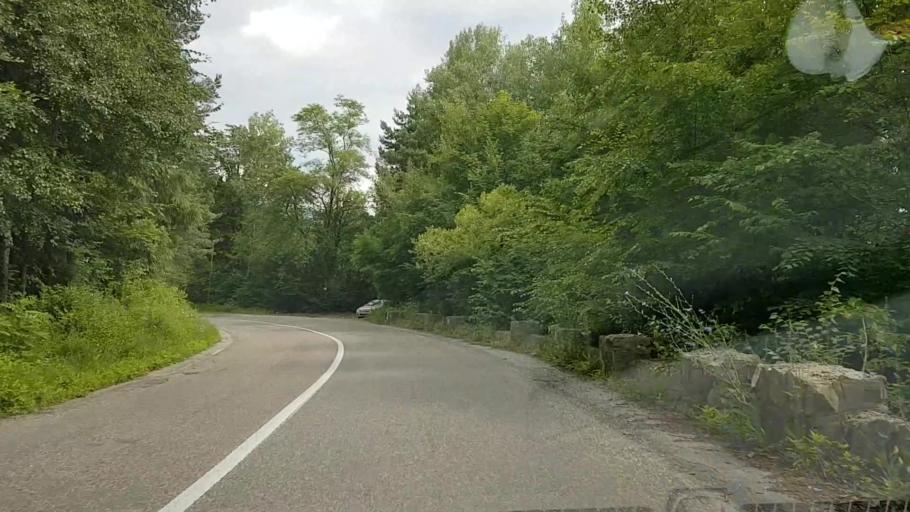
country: RO
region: Neamt
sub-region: Comuna Ceahlau
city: Ceahlau
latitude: 47.0540
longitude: 25.9739
